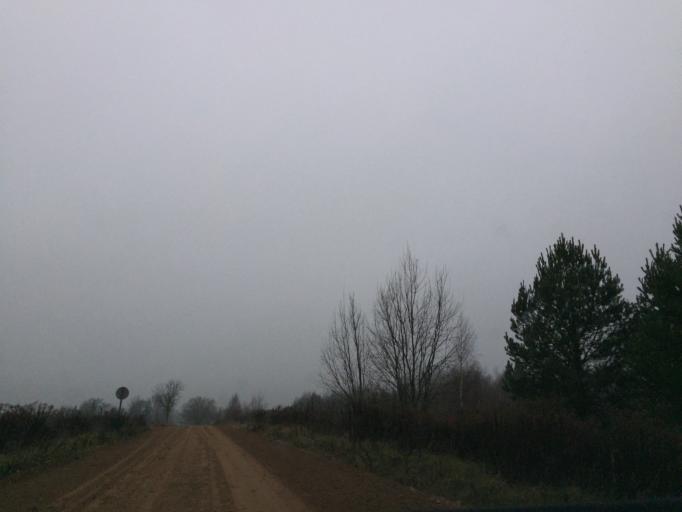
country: LV
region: Koceni
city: Koceni
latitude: 57.5164
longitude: 25.2966
